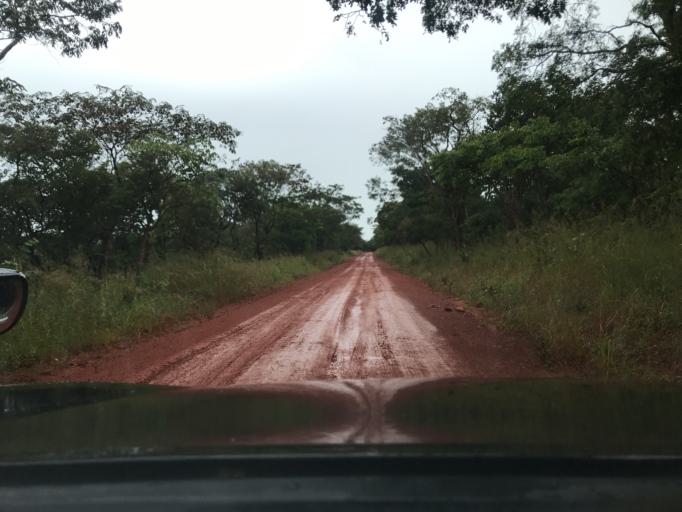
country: TZ
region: Kigoma
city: Uvinza
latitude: -5.2883
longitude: 30.3691
